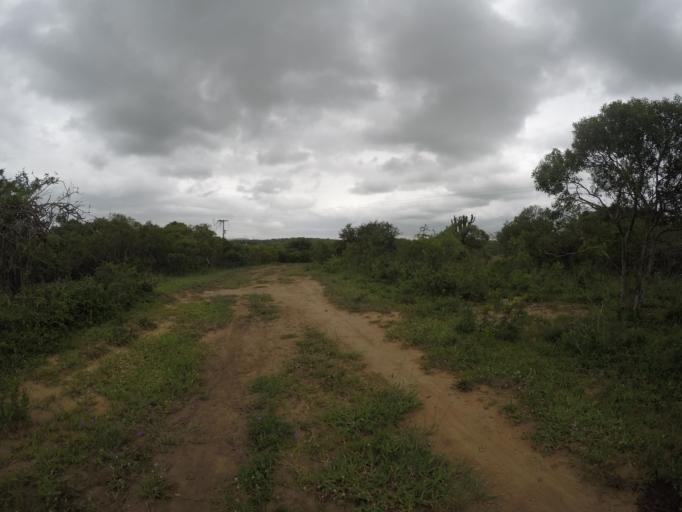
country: ZA
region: KwaZulu-Natal
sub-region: uThungulu District Municipality
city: Empangeni
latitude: -28.5928
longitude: 31.8462
